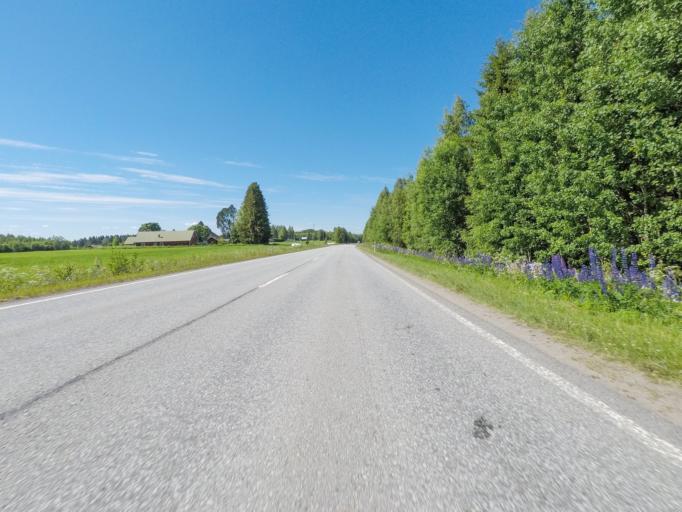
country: FI
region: Southern Savonia
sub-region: Savonlinna
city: Rantasalmi
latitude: 62.0283
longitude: 28.3473
